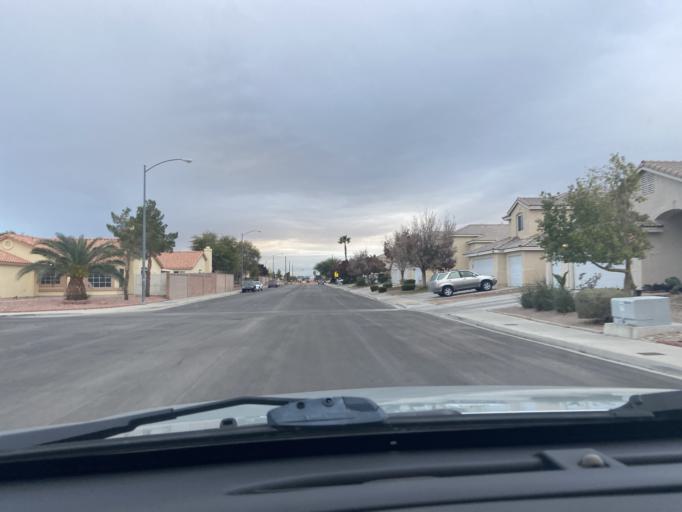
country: US
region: Nevada
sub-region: Clark County
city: Las Vegas
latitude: 36.2267
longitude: -115.1845
